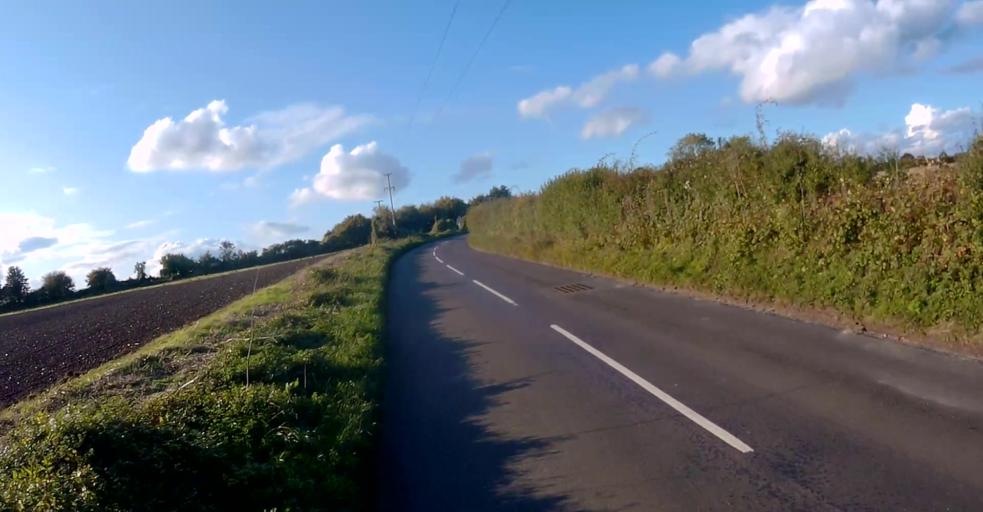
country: GB
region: England
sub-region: Hampshire
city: Odiham
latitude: 51.2466
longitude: -0.9345
